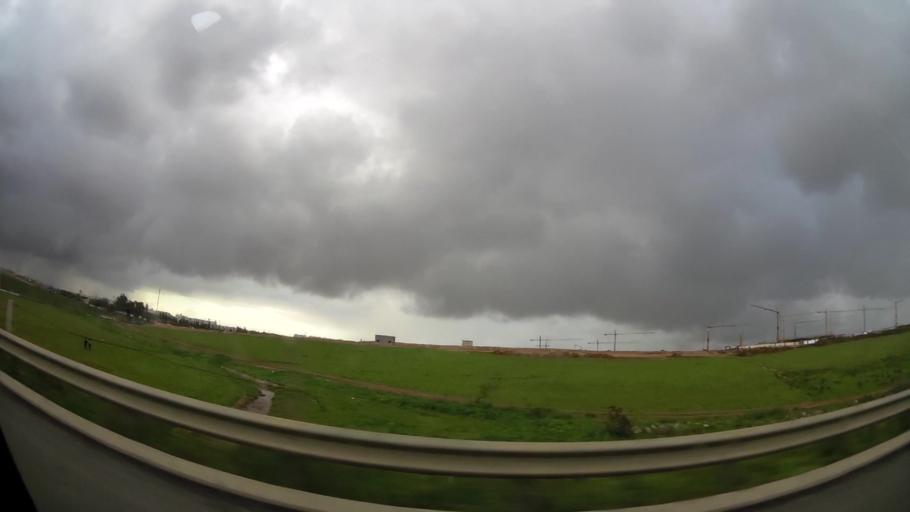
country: MA
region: Grand Casablanca
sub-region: Mediouna
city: Tit Mellil
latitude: 33.5658
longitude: -7.4812
